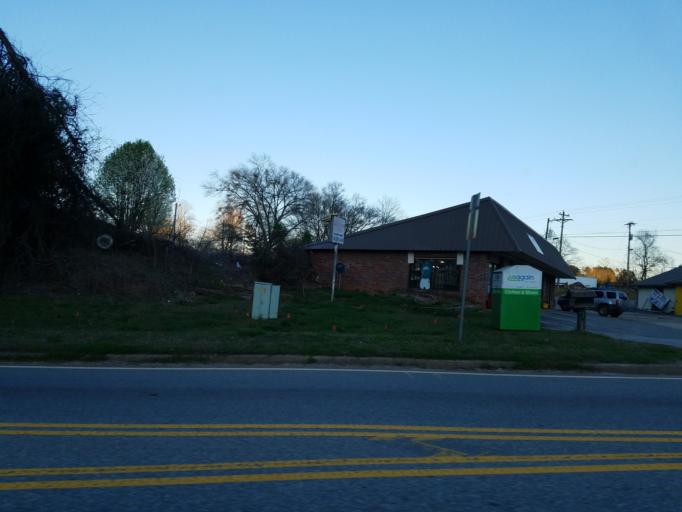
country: US
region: Georgia
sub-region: Dawson County
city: Dawsonville
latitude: 34.3412
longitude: -84.0230
